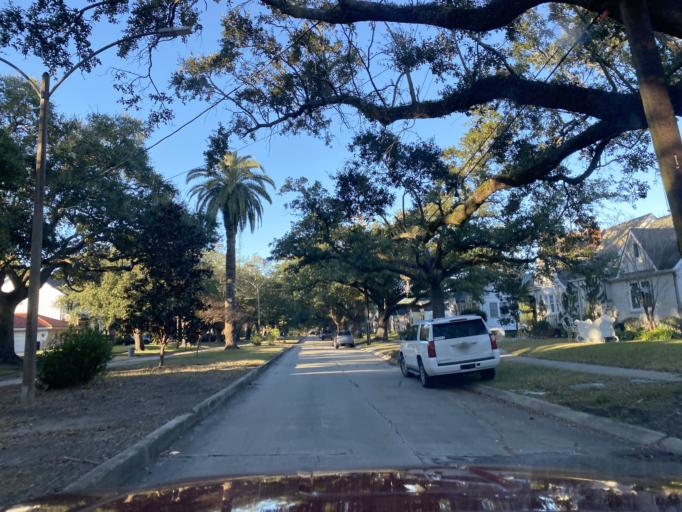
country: US
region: Louisiana
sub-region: Orleans Parish
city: New Orleans
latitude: 30.0069
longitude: -90.0553
